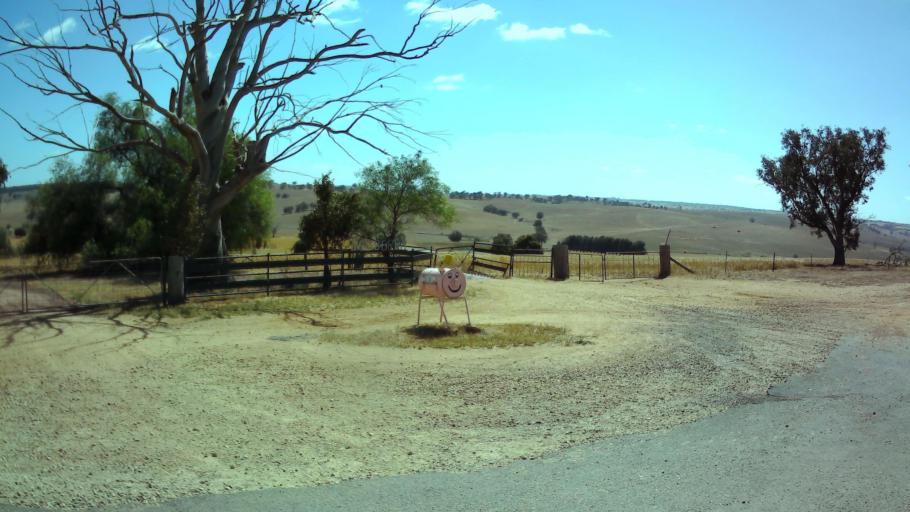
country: AU
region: New South Wales
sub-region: Weddin
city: Grenfell
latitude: -33.9534
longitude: 148.3992
